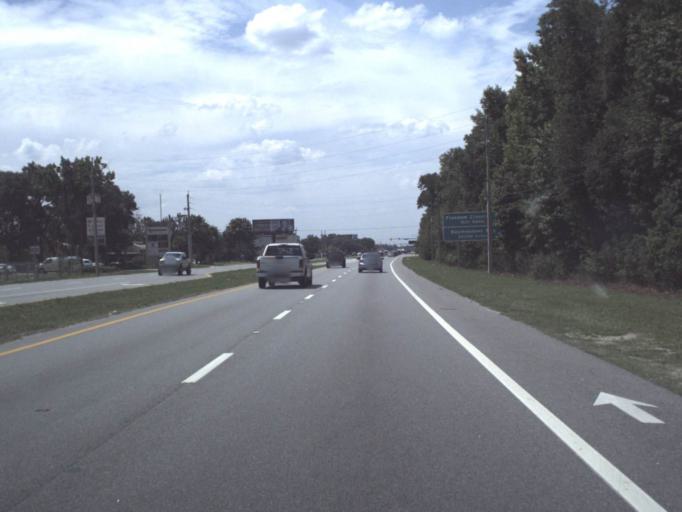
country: US
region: Florida
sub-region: Saint Johns County
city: Fruit Cove
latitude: 30.2106
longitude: -81.5798
